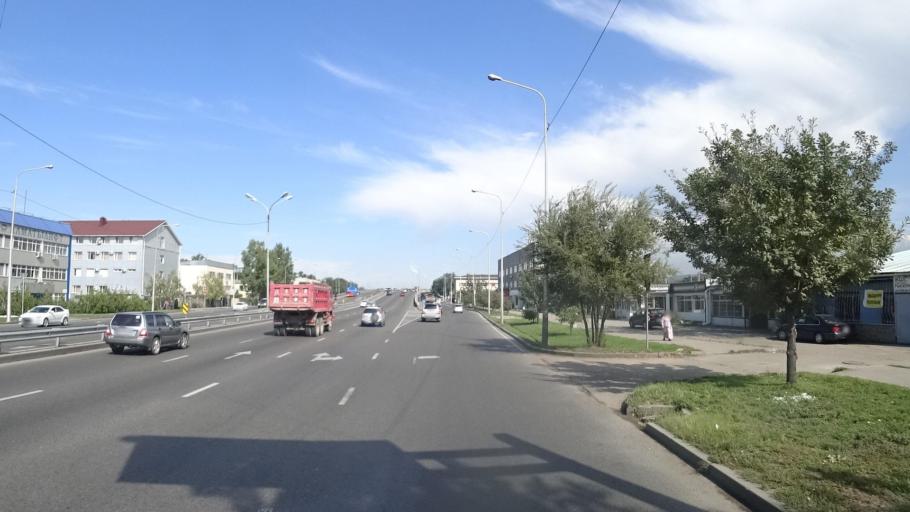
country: KZ
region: Almaty Qalasy
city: Almaty
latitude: 43.2914
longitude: 76.9307
